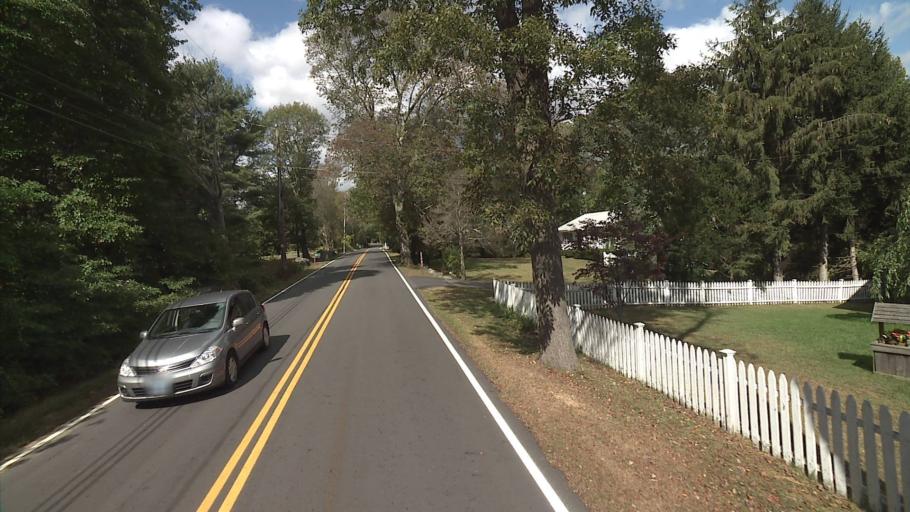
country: US
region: Connecticut
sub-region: New Haven County
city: Madison
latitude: 41.3911
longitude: -72.5999
